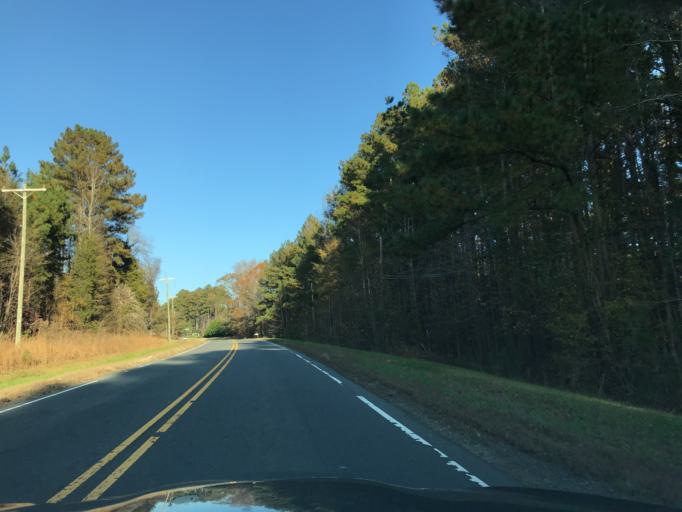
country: US
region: North Carolina
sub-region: Granville County
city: Butner
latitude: 36.0859
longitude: -78.7488
